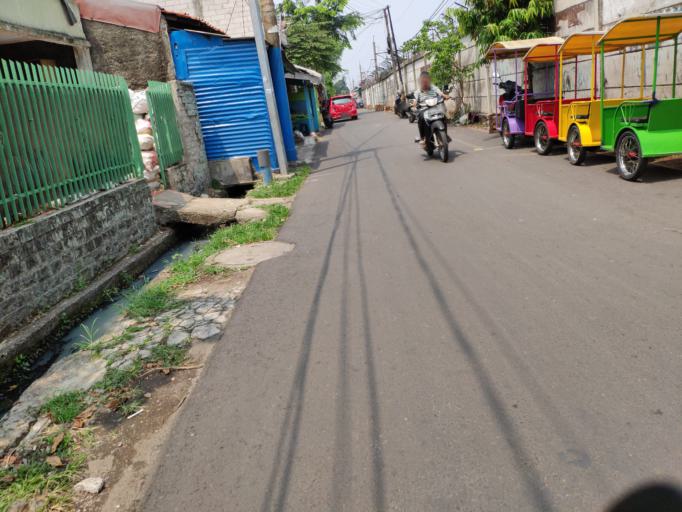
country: ID
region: Jakarta Raya
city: Jakarta
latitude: -6.2059
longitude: 106.8613
